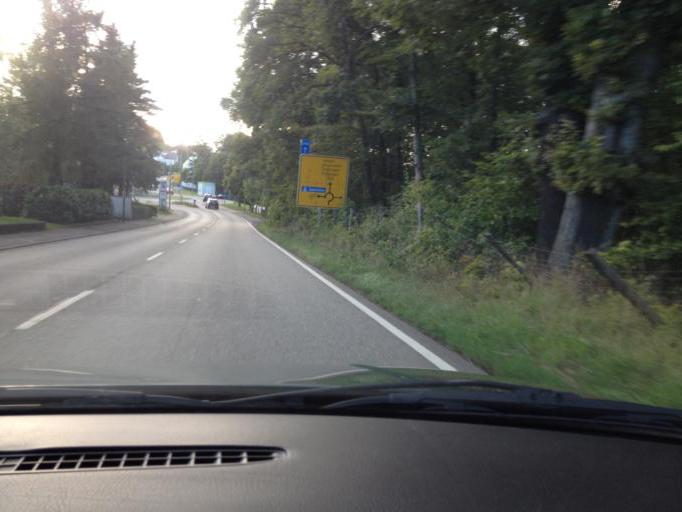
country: DE
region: Saarland
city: Riegelsberg
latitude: 49.2968
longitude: 6.9524
